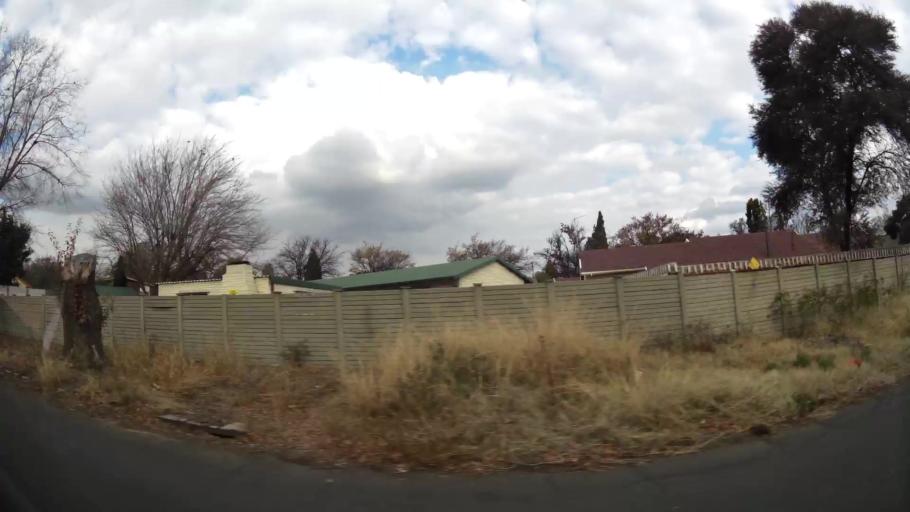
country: ZA
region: Orange Free State
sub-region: Fezile Dabi District Municipality
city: Sasolburg
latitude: -26.7949
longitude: 27.8110
